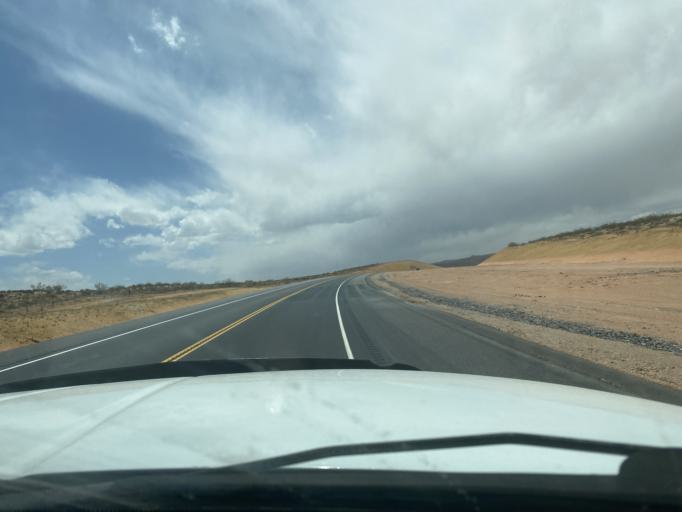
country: US
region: Utah
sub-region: Washington County
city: Hurricane
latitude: 37.1115
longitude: -113.3433
